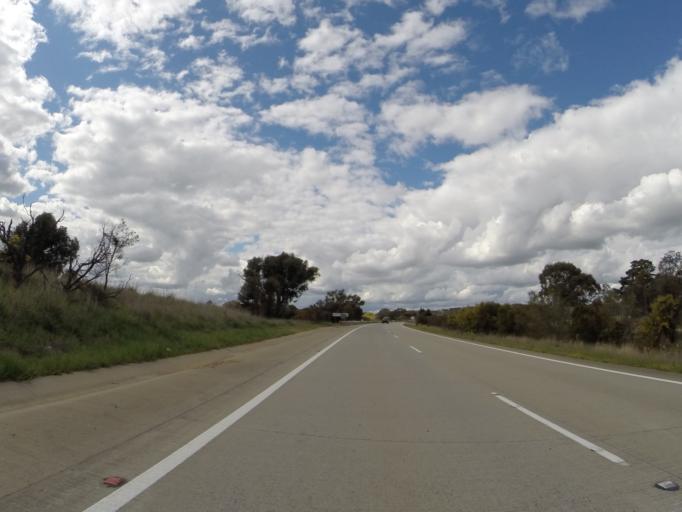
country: AU
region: New South Wales
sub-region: Yass Valley
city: Murrumbateman
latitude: -34.8047
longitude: 149.1336
